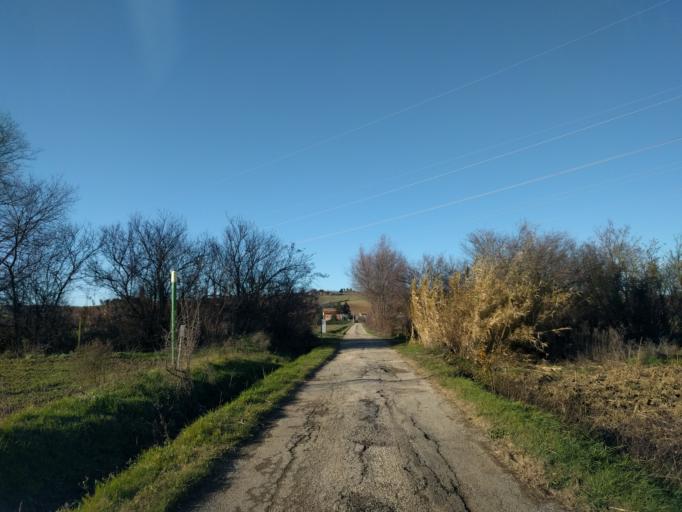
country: IT
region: The Marches
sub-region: Provincia di Pesaro e Urbino
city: Cuccurano
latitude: 43.7844
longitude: 12.9512
